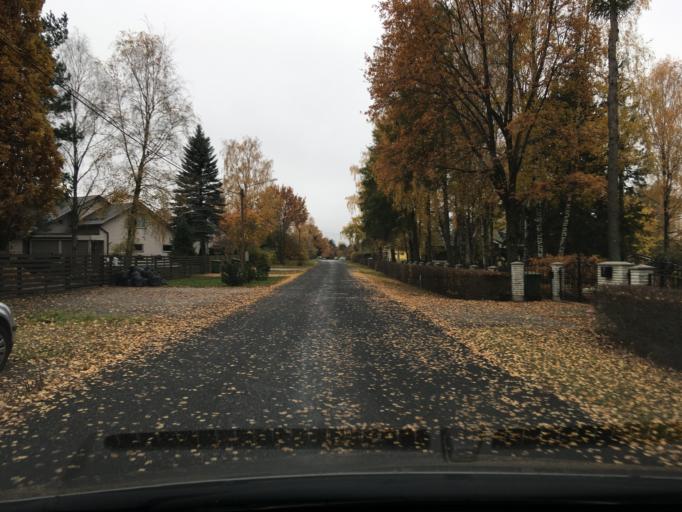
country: EE
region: Tartu
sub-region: Tartu linn
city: Tartu
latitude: 58.3495
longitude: 26.7777
